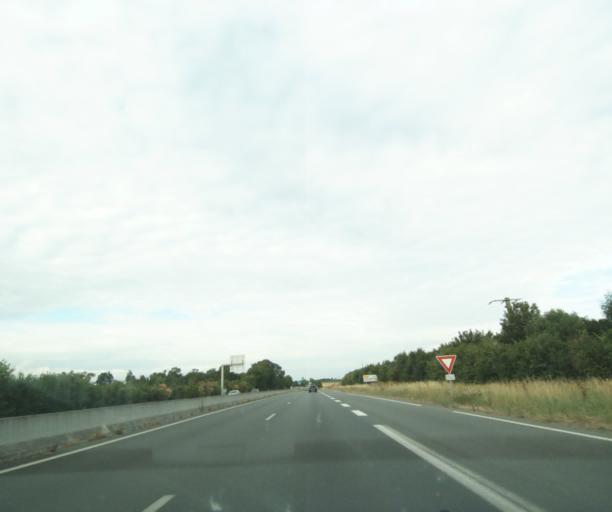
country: FR
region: Poitou-Charentes
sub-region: Departement de la Charente-Maritime
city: Dompierre-sur-Mer
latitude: 46.1817
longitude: -1.0877
